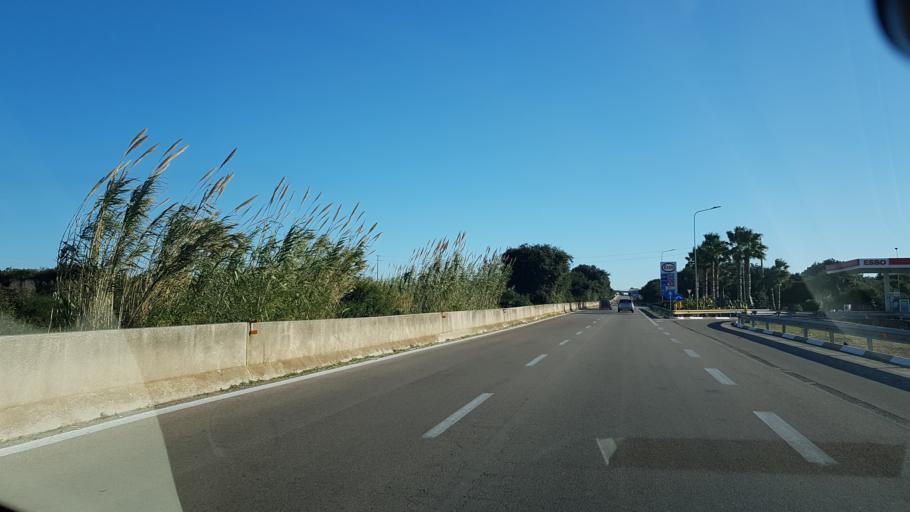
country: IT
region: Apulia
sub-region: Provincia di Lecce
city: Alezio
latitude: 40.0183
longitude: 18.0443
